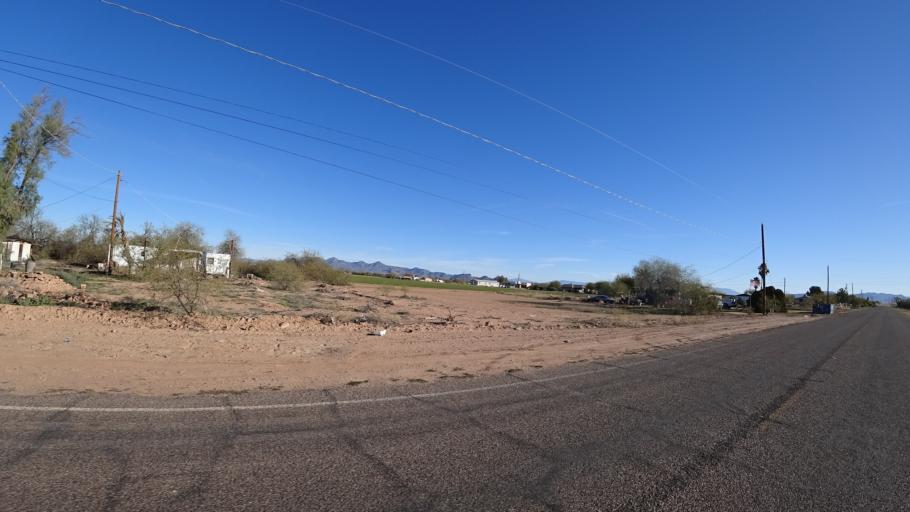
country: US
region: Arizona
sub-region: Maricopa County
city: Scottsdale
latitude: 33.4805
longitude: -111.8540
